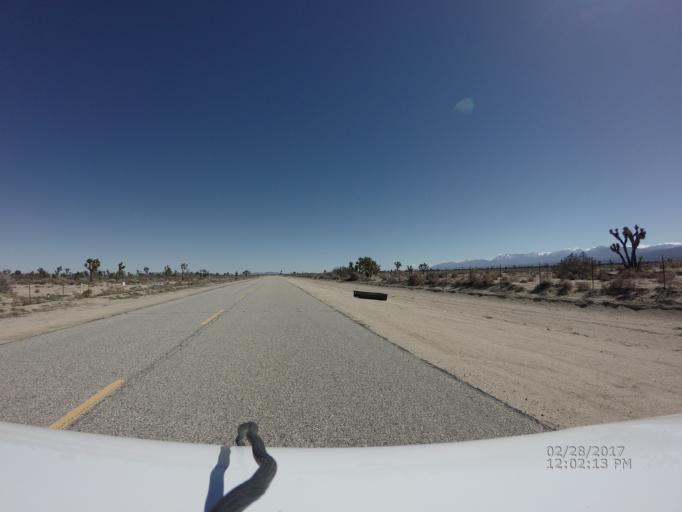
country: US
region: California
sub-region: Los Angeles County
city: Palmdale
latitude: 34.5947
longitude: -118.0456
